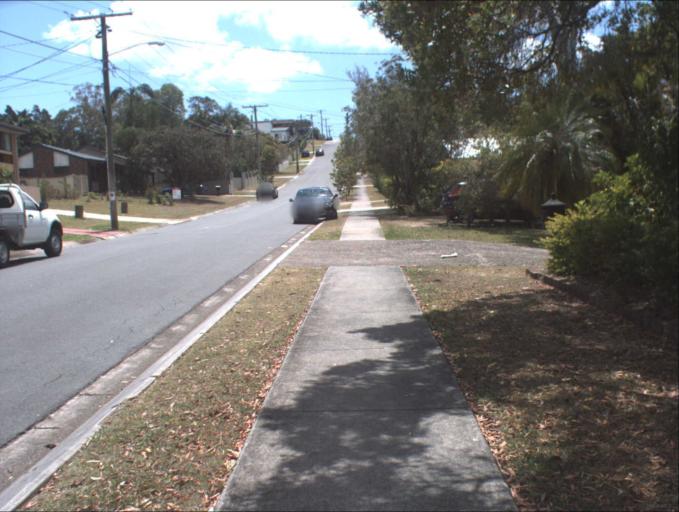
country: AU
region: Queensland
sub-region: Logan
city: Slacks Creek
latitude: -27.6539
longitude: 153.1711
